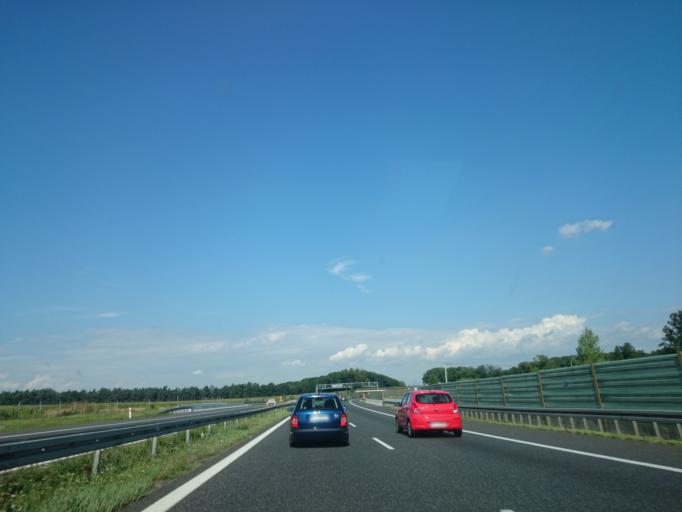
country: PL
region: Silesian Voivodeship
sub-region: Powiat gliwicki
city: Rudziniec
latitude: 50.3798
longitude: 18.4683
